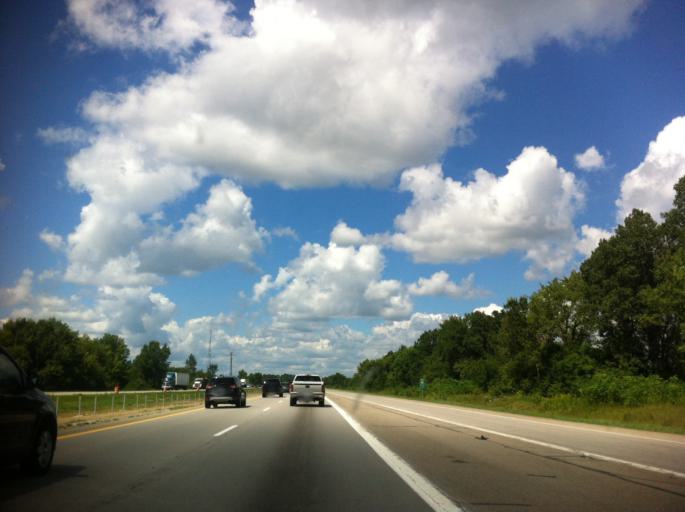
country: US
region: Michigan
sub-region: Washtenaw County
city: Milan
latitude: 42.1606
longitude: -83.6840
